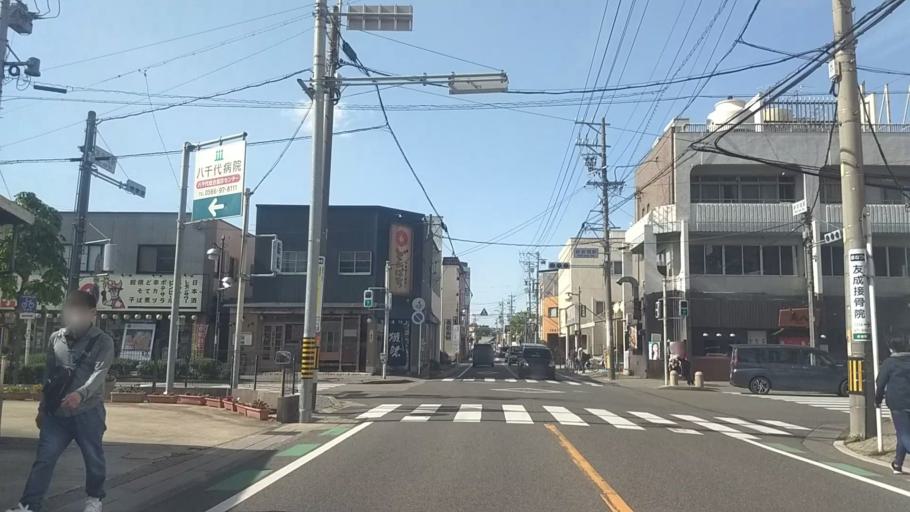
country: JP
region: Aichi
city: Anjo
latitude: 34.9864
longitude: 137.0840
